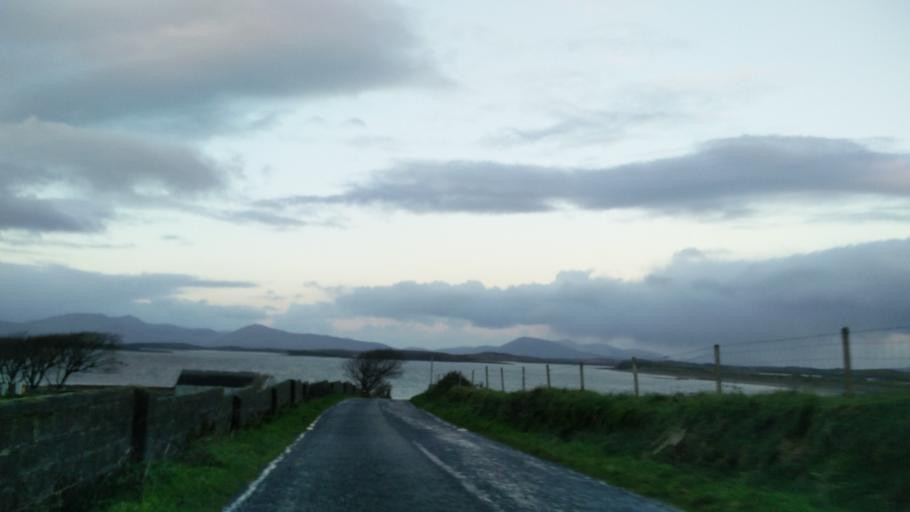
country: IE
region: Connaught
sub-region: Maigh Eo
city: Westport
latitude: 53.7861
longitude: -9.6660
